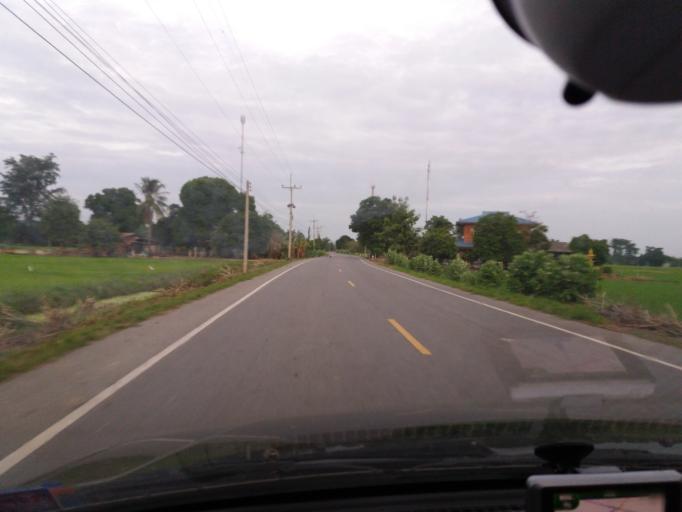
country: TH
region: Suphan Buri
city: Don Chedi
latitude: 14.7065
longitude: 100.0301
